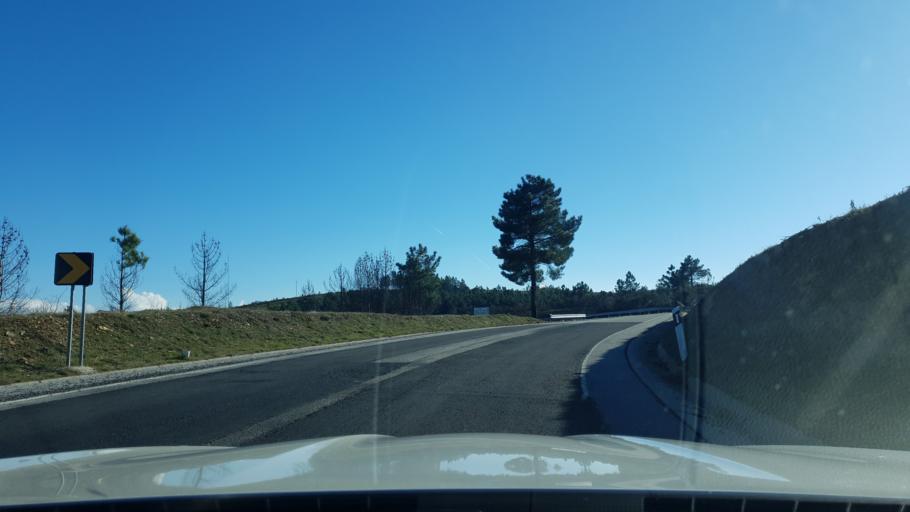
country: PT
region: Braganca
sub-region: Freixo de Espada A Cinta
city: Freixo de Espada a Cinta
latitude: 41.1575
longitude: -6.7987
